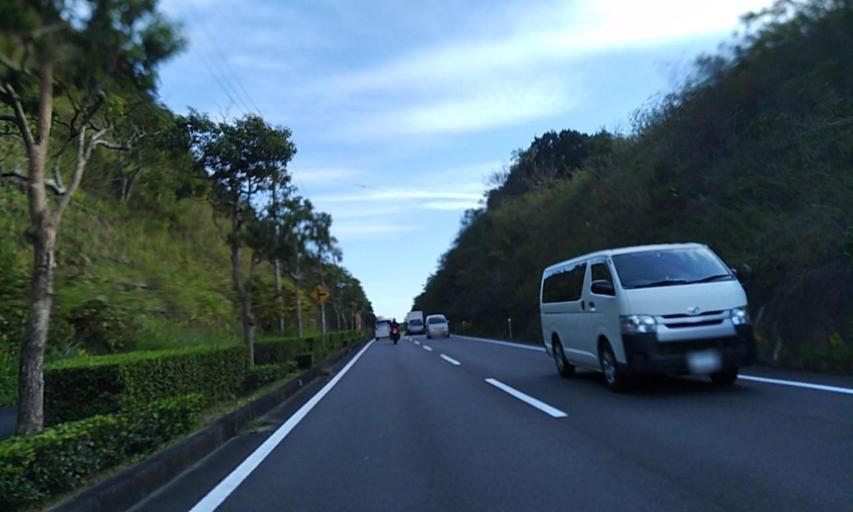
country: JP
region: Mie
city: Toba
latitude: 34.3566
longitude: 136.8056
